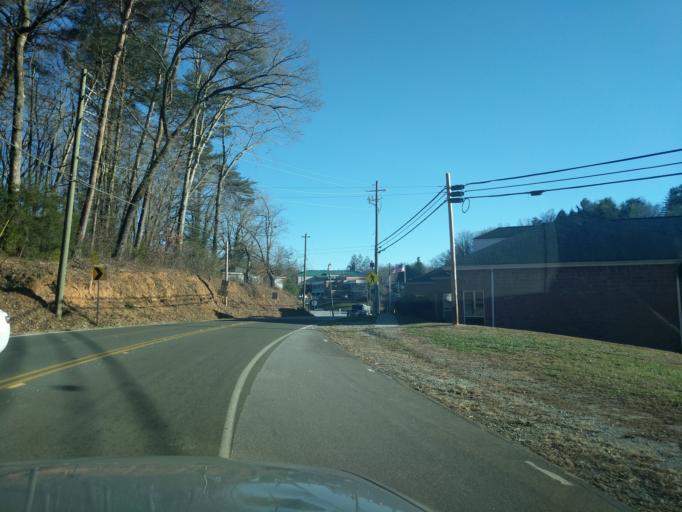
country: US
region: Georgia
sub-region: Rabun County
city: Clayton
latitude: 34.8808
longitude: -83.4058
